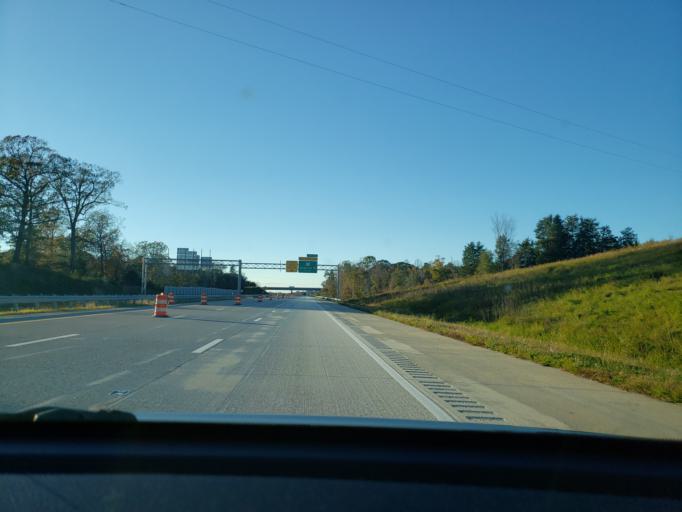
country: US
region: North Carolina
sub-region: Forsyth County
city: Walkertown
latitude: 36.1385
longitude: -80.1407
